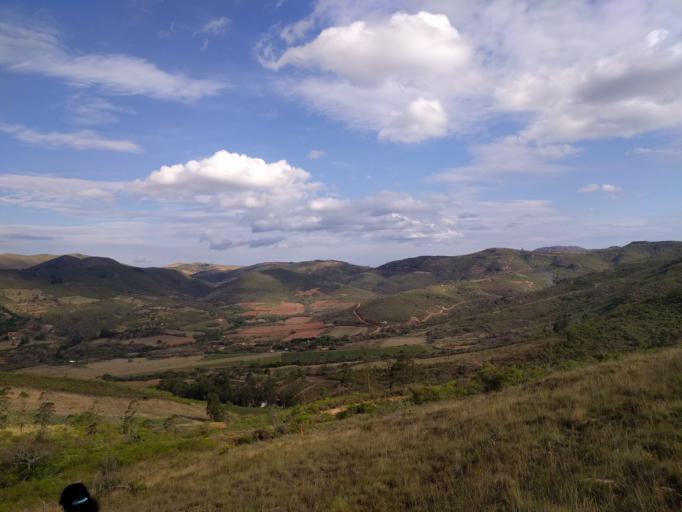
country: BO
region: Santa Cruz
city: Samaipata
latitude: -18.1887
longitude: -63.8869
